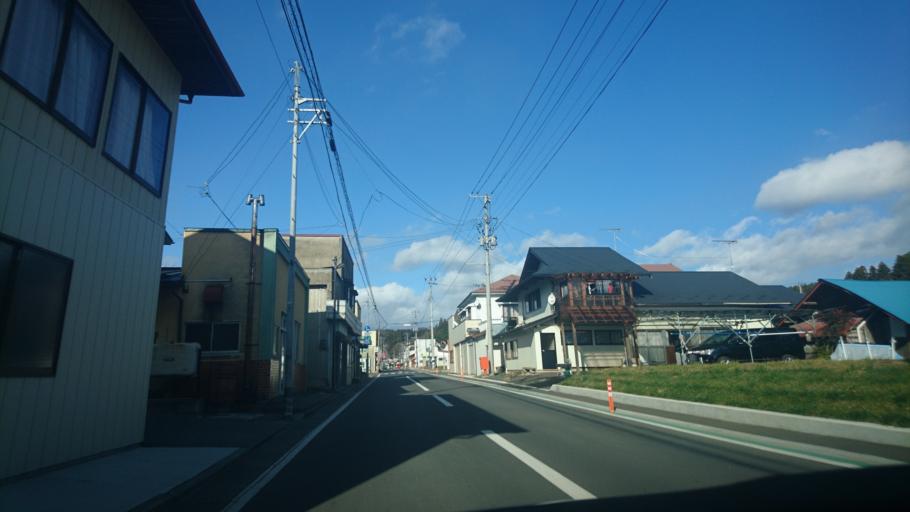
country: JP
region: Iwate
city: Mizusawa
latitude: 39.0503
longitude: 141.3668
